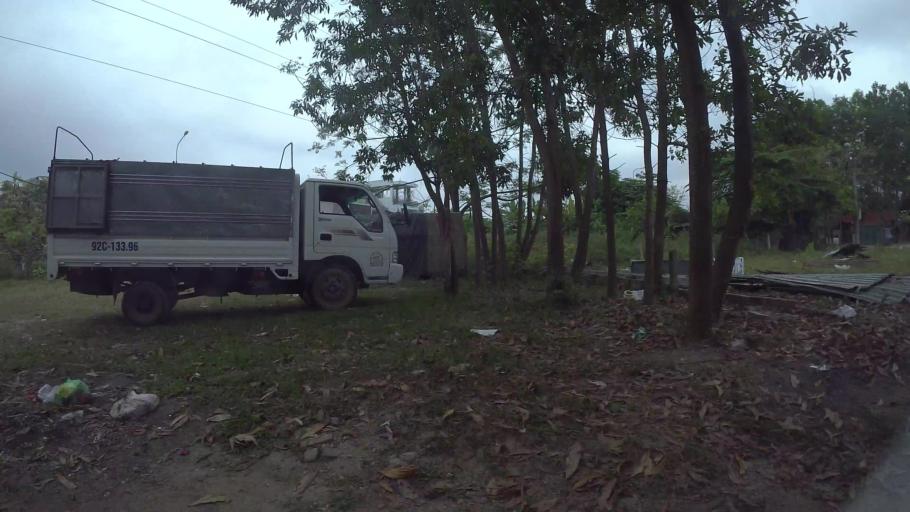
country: VN
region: Da Nang
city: Thanh Khe
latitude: 16.0435
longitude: 108.1740
